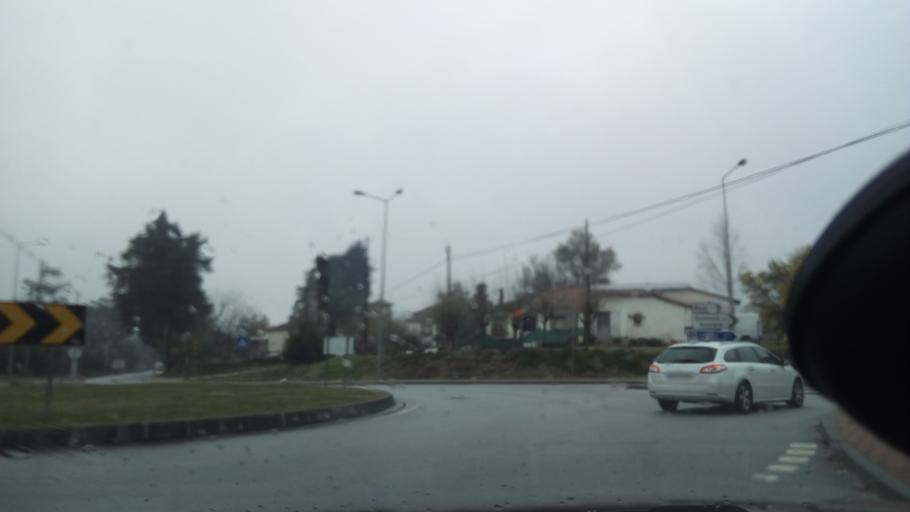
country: PT
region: Viseu
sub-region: Mangualde
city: Mangualde
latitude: 40.6081
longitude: -7.7281
